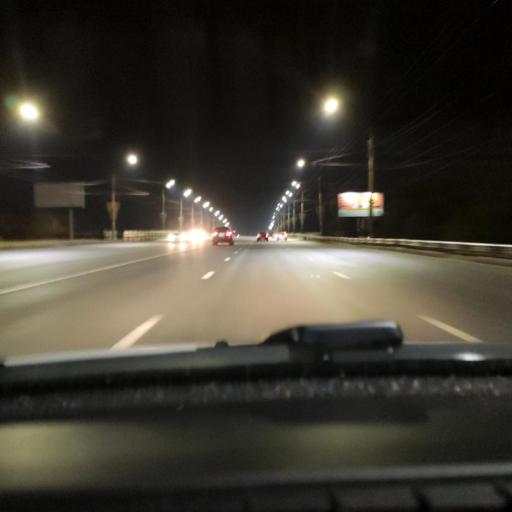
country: RU
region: Voronezj
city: Voronezh
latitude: 51.6332
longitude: 39.2261
